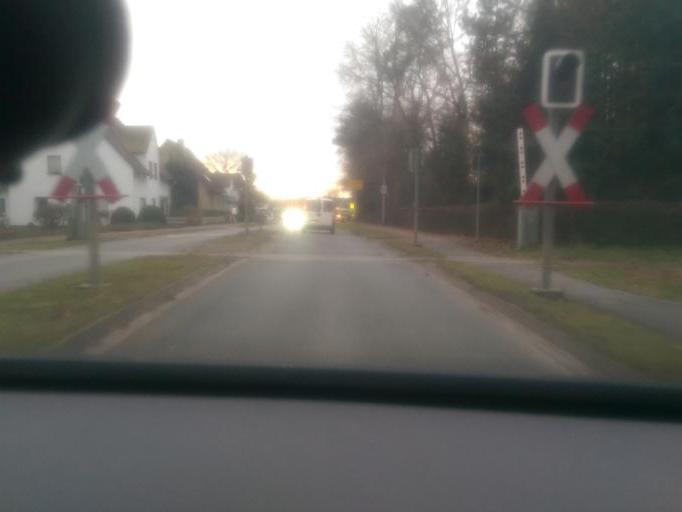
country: DE
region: North Rhine-Westphalia
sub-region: Regierungsbezirk Detmold
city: Hovelhof
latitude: 51.8286
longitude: 8.6567
